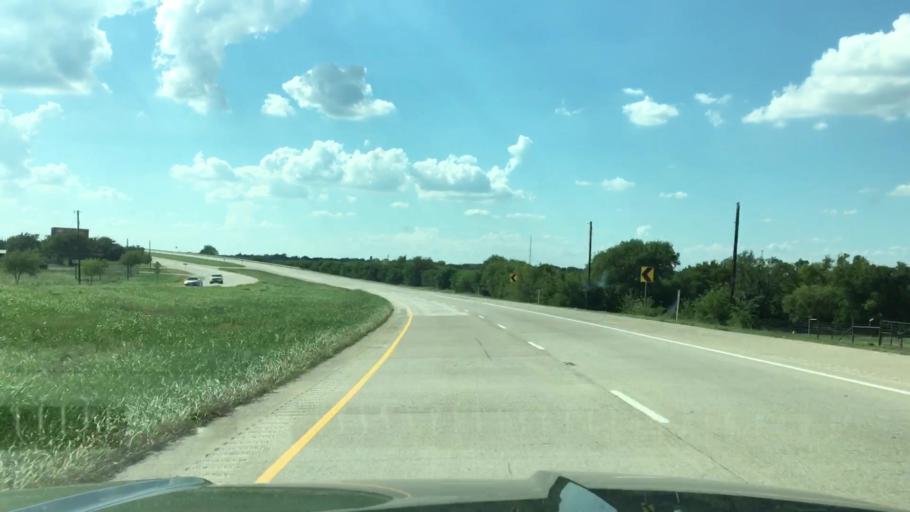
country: US
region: Texas
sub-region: Wise County
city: Rhome
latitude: 33.0453
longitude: -97.4537
